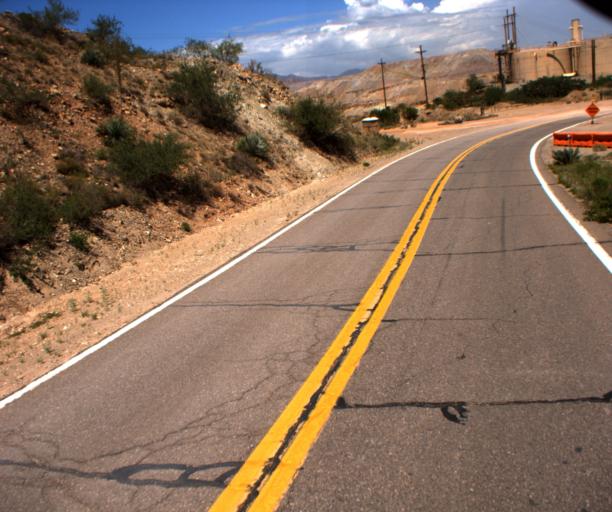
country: US
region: Arizona
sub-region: Greenlee County
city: Morenci
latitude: 33.0718
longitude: -109.3692
